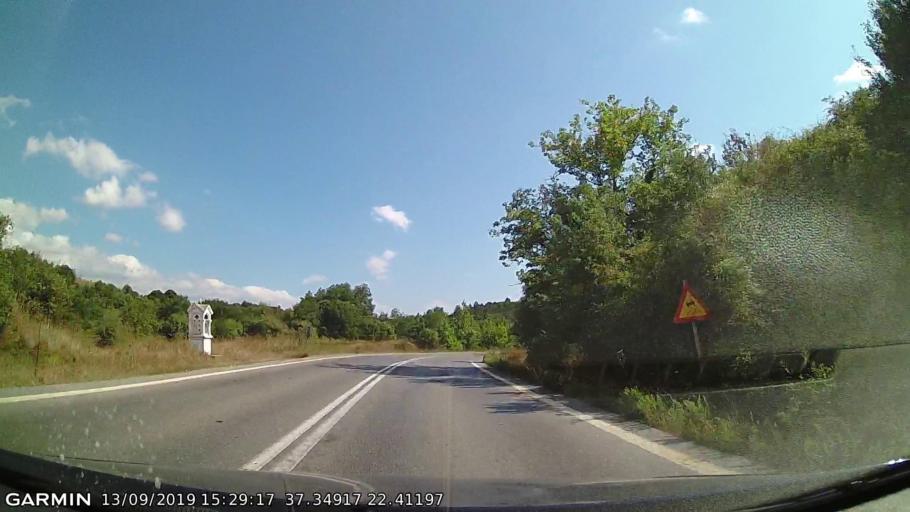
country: GR
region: Peloponnese
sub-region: Nomos Lakonias
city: Kariai
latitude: 37.3491
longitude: 22.4121
